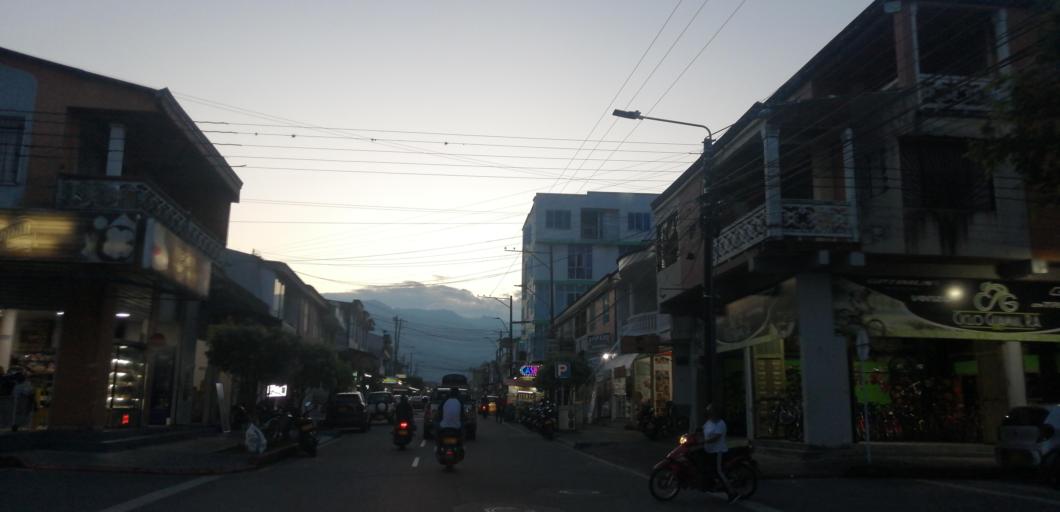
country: CO
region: Meta
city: Acacias
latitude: 3.9878
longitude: -73.7704
